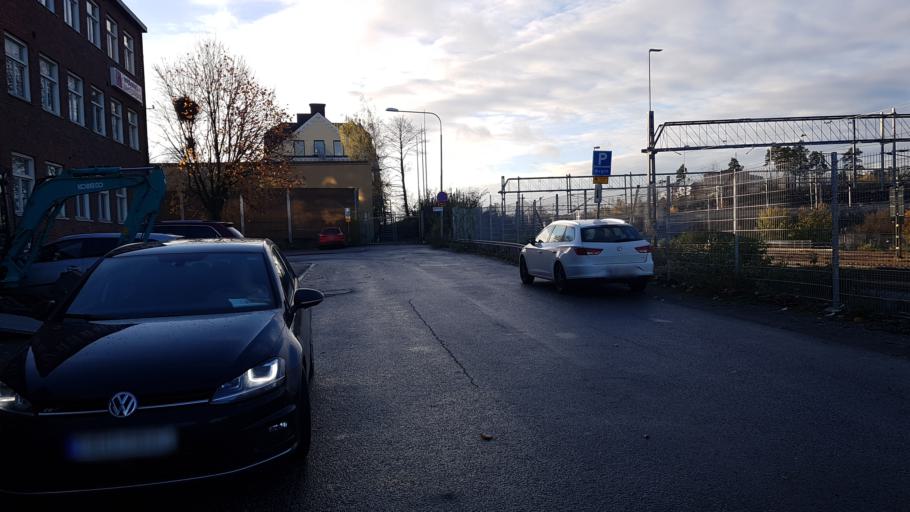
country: SE
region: Stockholm
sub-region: Solna Kommun
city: Solna
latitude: 59.3568
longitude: 18.0134
